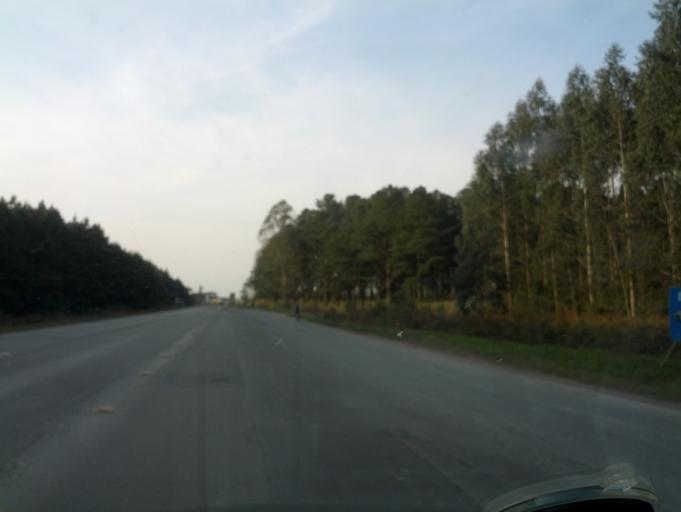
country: BR
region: Santa Catarina
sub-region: Otacilio Costa
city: Otacilio Costa
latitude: -27.5115
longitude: -50.1308
